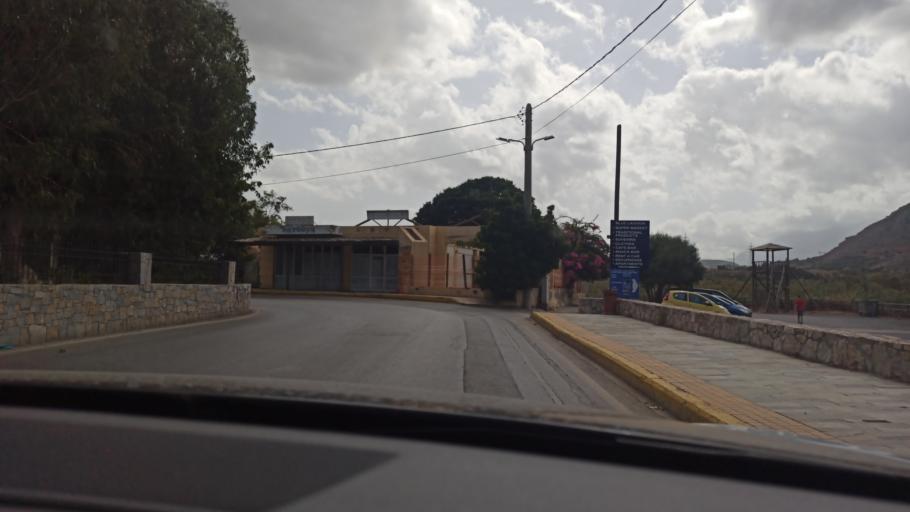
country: GR
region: Crete
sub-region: Nomos Irakleiou
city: Gazi
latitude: 35.3373
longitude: 25.0561
